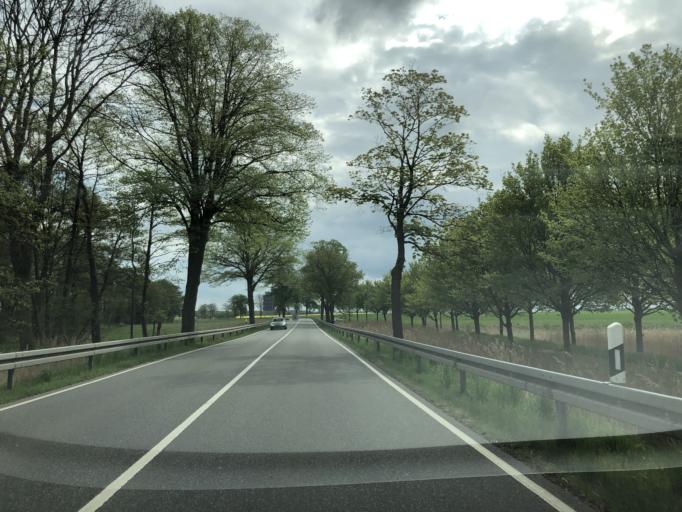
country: DE
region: Mecklenburg-Vorpommern
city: Plau am See
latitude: 53.4627
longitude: 12.1544
